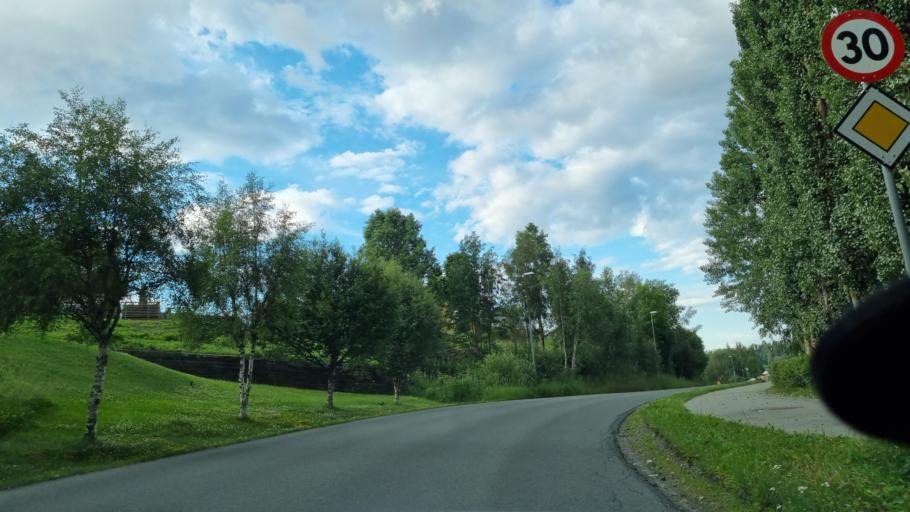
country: NO
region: Sor-Trondelag
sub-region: Trondheim
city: Trondheim
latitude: 63.3845
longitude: 10.3272
